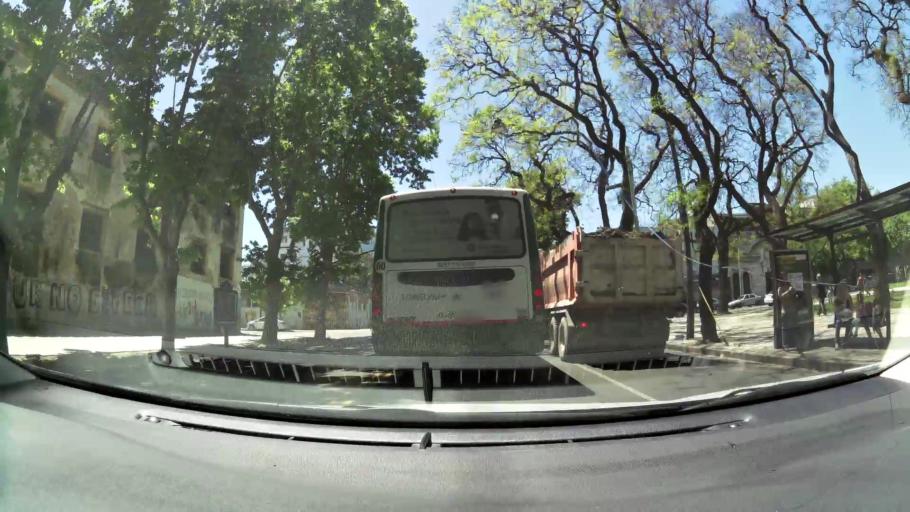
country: AR
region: Buenos Aires F.D.
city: Buenos Aires
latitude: -34.6350
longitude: -58.3943
